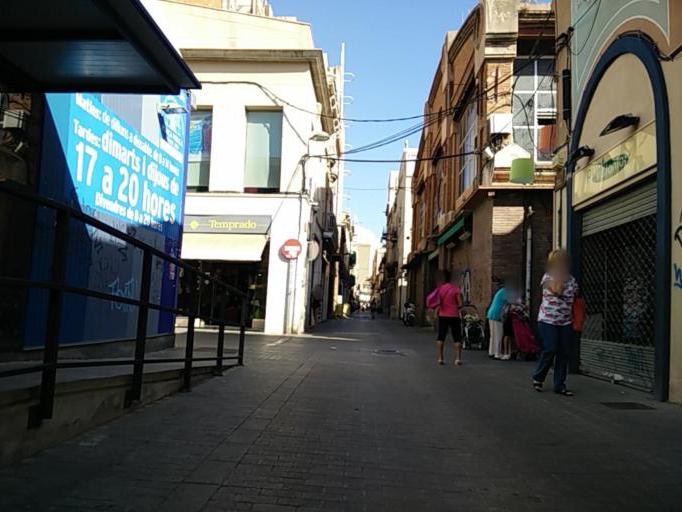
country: ES
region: Catalonia
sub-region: Provincia de Barcelona
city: Badalona
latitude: 41.4480
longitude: 2.2475
